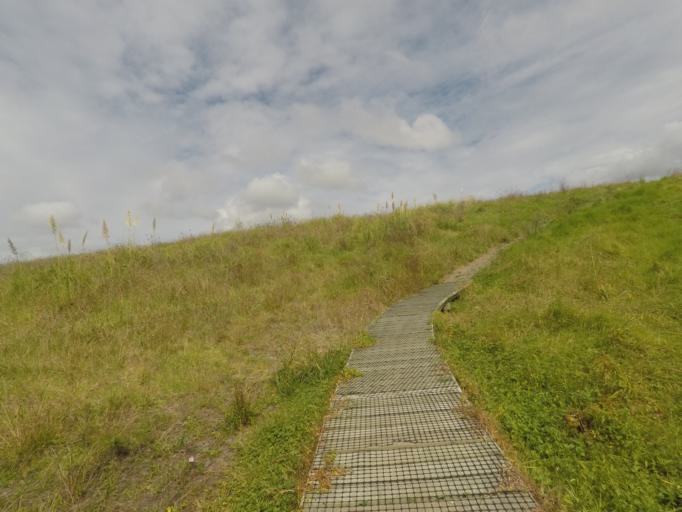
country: NZ
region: Auckland
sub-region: Auckland
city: Rothesay Bay
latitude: -36.6537
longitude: 174.7215
